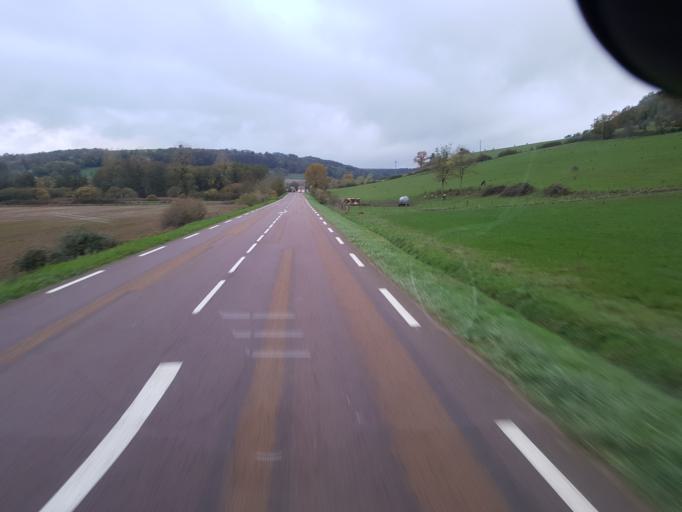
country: FR
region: Bourgogne
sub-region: Departement de la Cote-d'Or
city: Chatillon-sur-Seine
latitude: 47.6765
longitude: 4.6783
